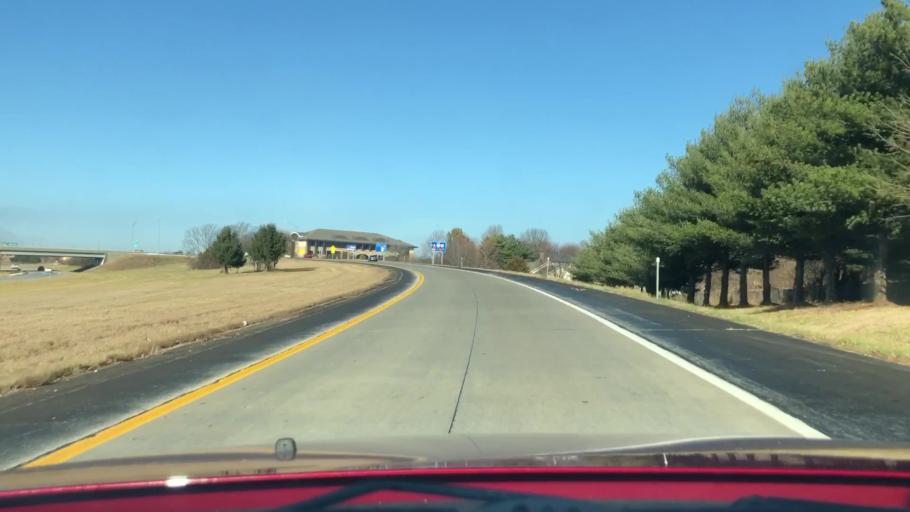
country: US
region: Missouri
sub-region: Greene County
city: Battlefield
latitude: 37.1420
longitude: -93.3158
